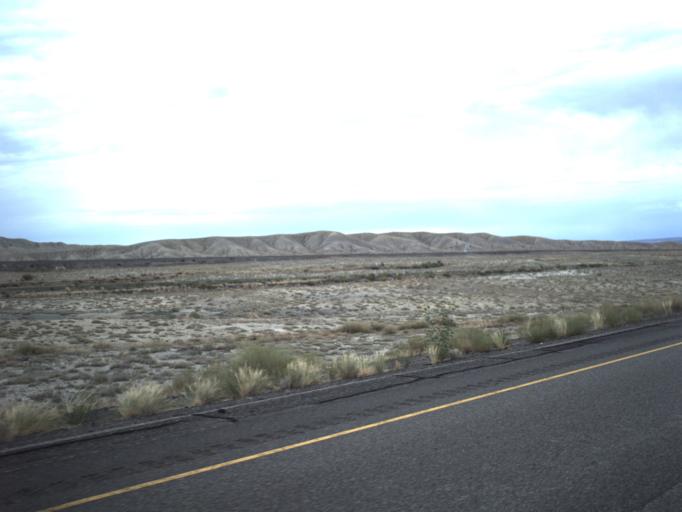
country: US
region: Utah
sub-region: Grand County
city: Moab
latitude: 38.9353
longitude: -109.4684
